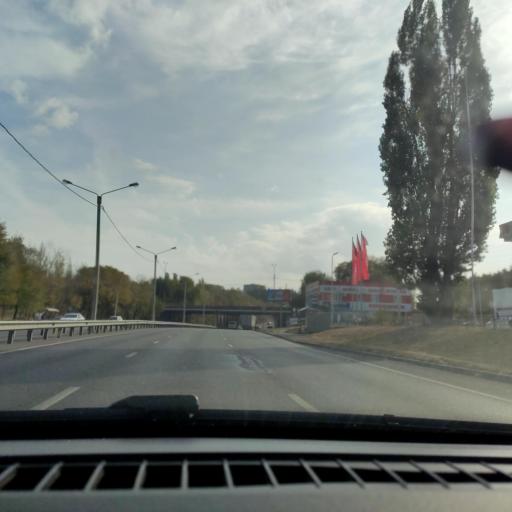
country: RU
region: Voronezj
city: Voronezh
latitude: 51.6566
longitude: 39.1352
